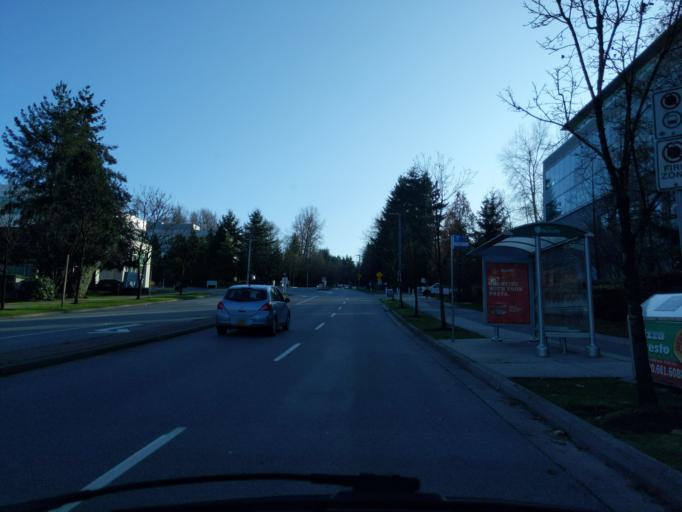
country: CA
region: British Columbia
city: Burnaby
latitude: 49.2543
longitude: -123.0108
